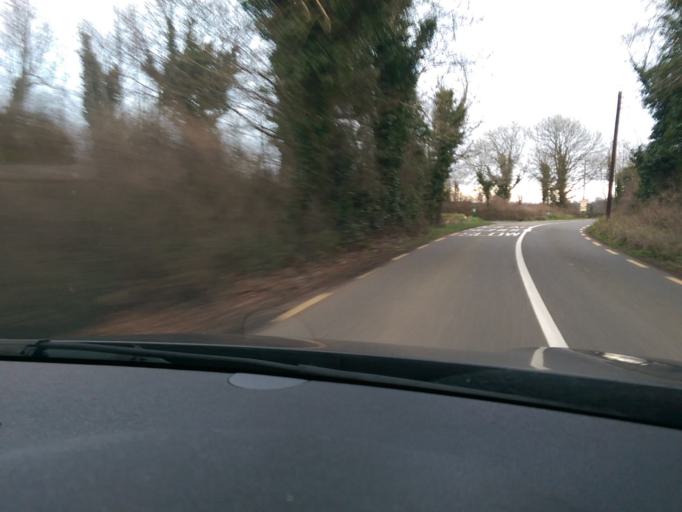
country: IE
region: Connaught
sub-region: Sligo
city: Ballymote
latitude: 54.0037
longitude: -8.5400
